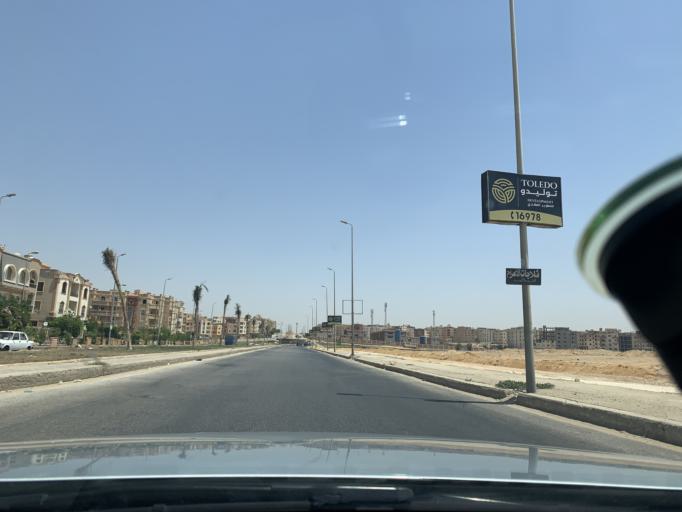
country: EG
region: Muhafazat al Qahirah
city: Cairo
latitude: 29.9993
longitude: 31.4652
